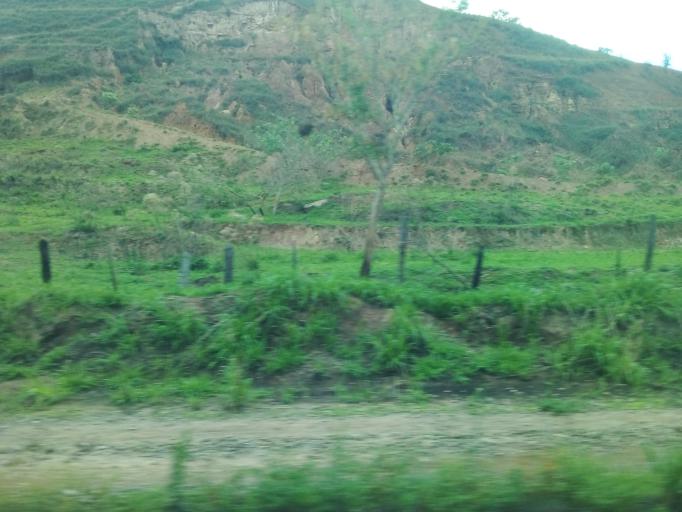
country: BR
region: Minas Gerais
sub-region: Governador Valadares
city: Governador Valadares
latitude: -19.0709
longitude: -42.1516
